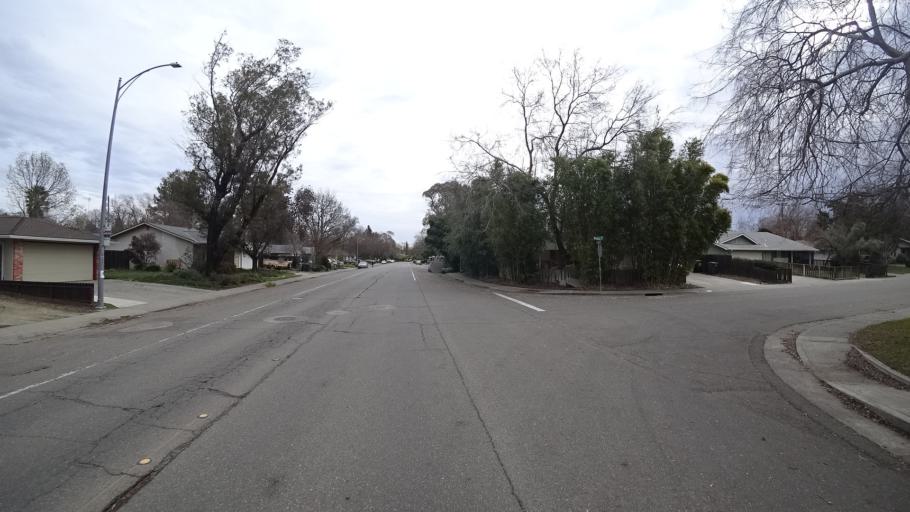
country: US
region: California
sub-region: Yolo County
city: Davis
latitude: 38.5578
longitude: -121.7206
